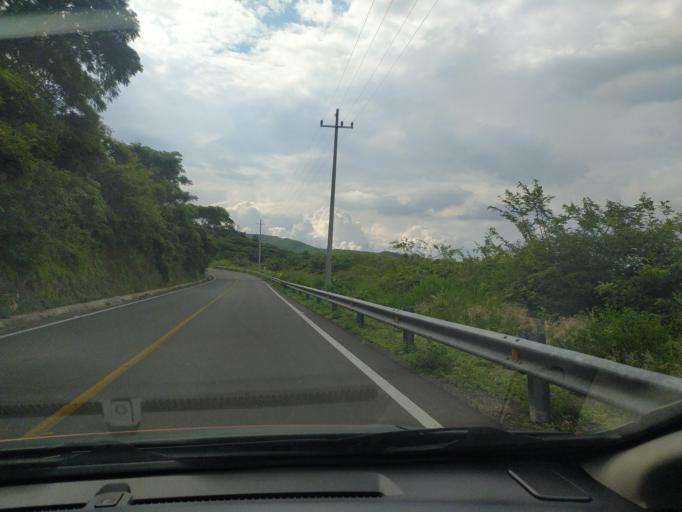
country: MX
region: Jalisco
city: Villa Corona
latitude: 20.3928
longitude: -103.6747
